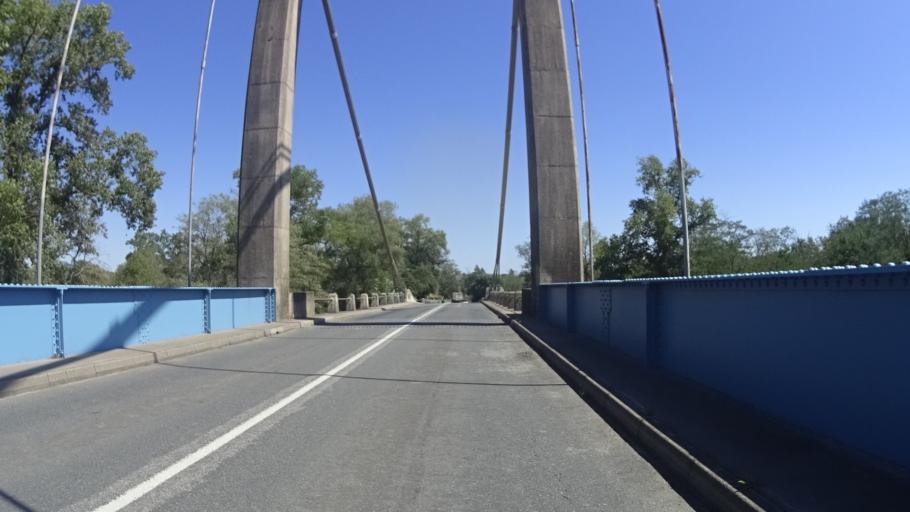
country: FR
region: Centre
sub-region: Departement du Loiret
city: Bonny-sur-Loire
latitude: 47.5508
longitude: 2.8370
